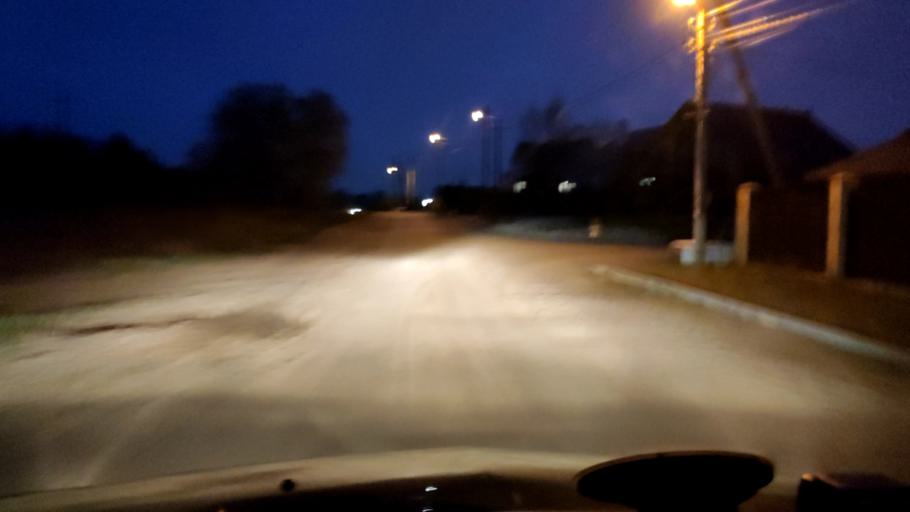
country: RU
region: Voronezj
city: Pridonskoy
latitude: 51.6337
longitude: 39.0860
